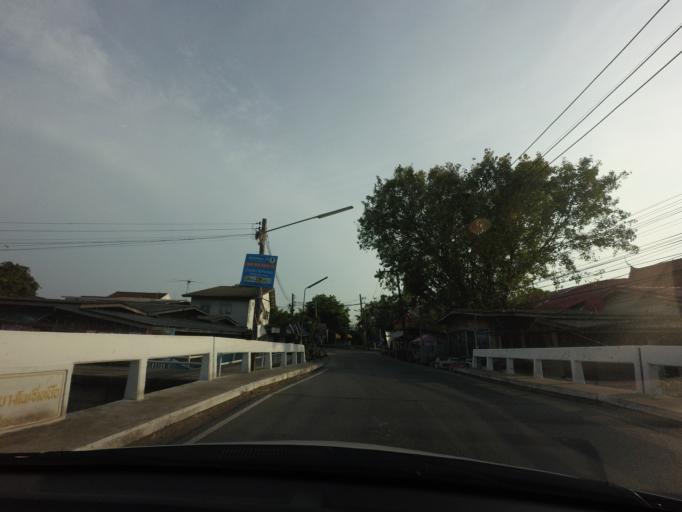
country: TH
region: Pathum Thani
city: Pathum Thani
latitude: 14.0311
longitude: 100.5397
